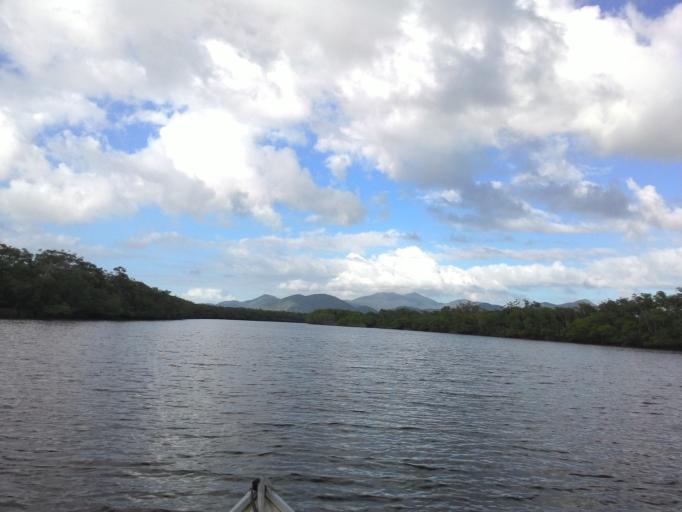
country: BR
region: Sao Paulo
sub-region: Pariquera-Acu
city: Pariquera Acu
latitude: -24.8298
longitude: -47.7392
